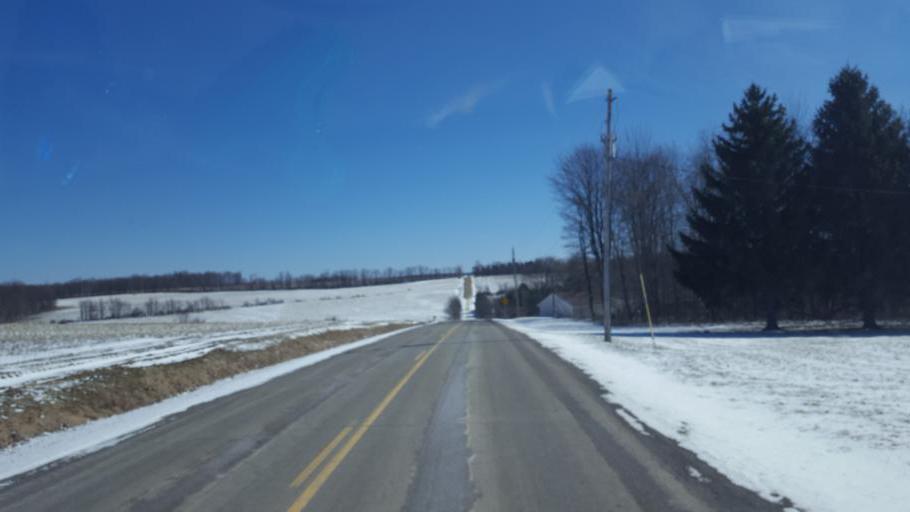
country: US
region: New York
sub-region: Allegany County
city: Andover
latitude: 42.0608
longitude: -77.7954
